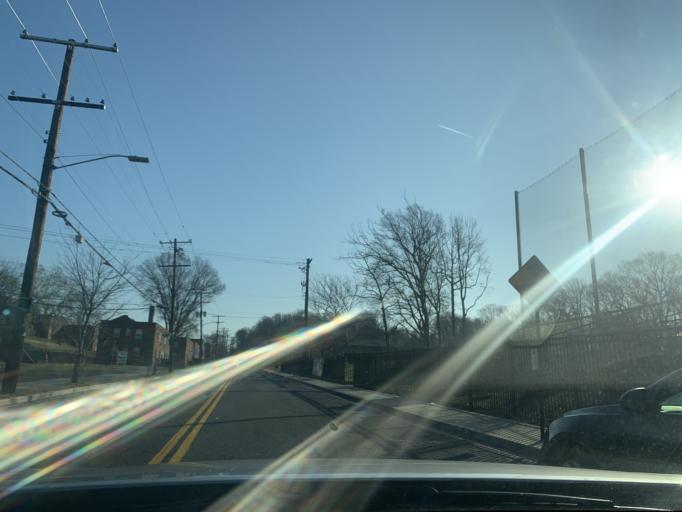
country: US
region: Maryland
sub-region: Prince George's County
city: Coral Hills
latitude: 38.8834
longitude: -76.9522
